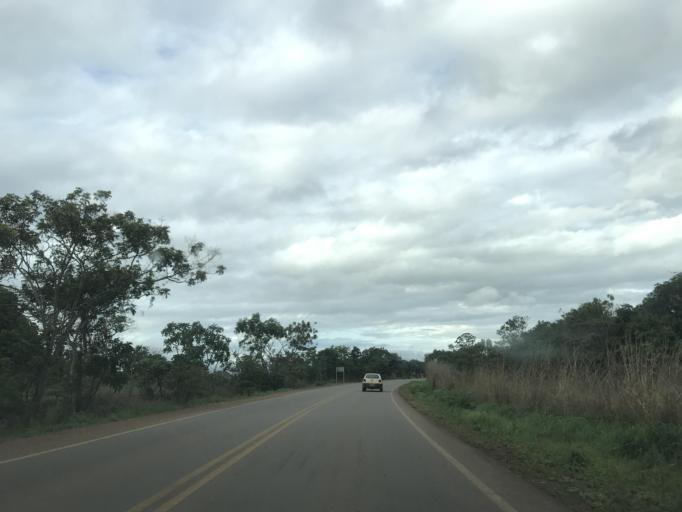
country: BR
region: Goias
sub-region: Vianopolis
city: Vianopolis
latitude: -16.7342
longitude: -48.4456
